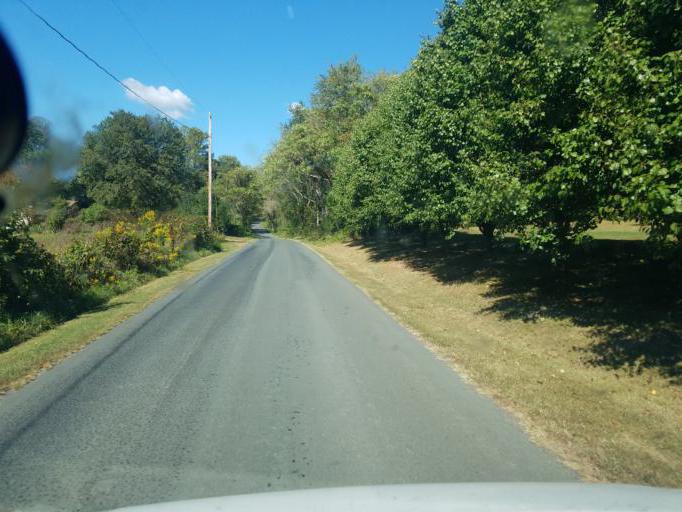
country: US
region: Virginia
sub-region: Greene County
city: Stanardsville
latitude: 38.3497
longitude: -78.4022
